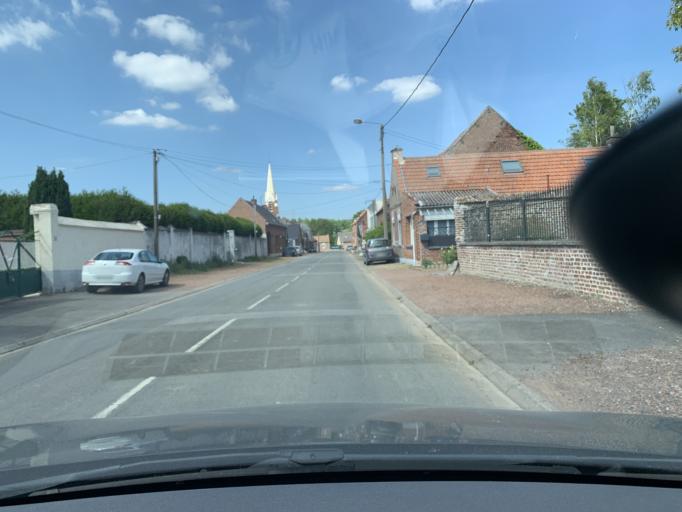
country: FR
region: Nord-Pas-de-Calais
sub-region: Departement du Pas-de-Calais
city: Marquion
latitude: 50.2347
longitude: 3.0968
